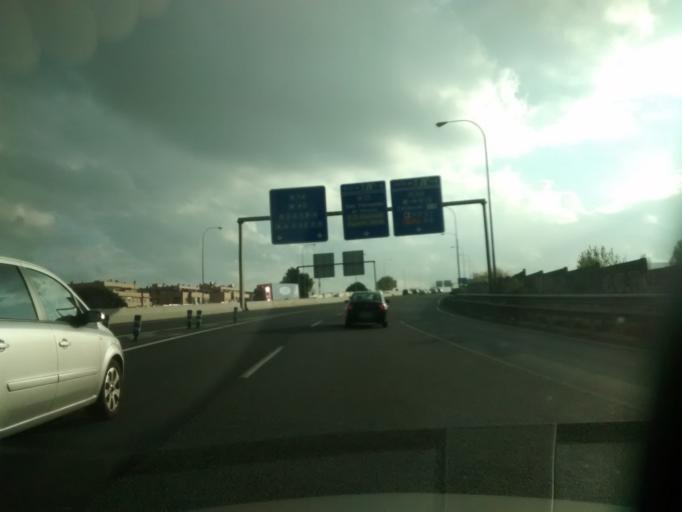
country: ES
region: Madrid
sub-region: Provincia de Madrid
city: San Blas
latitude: 40.4467
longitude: -3.5901
